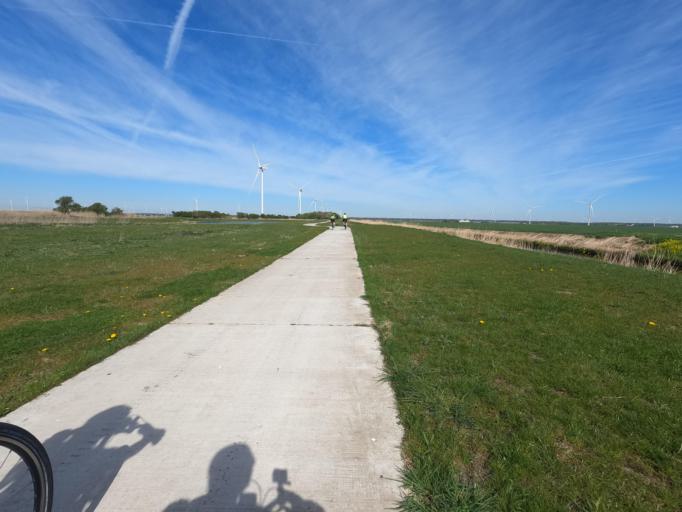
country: NL
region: Utrecht
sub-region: Gemeente Bunschoten
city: Spakenburg
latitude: 52.3476
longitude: 5.4060
